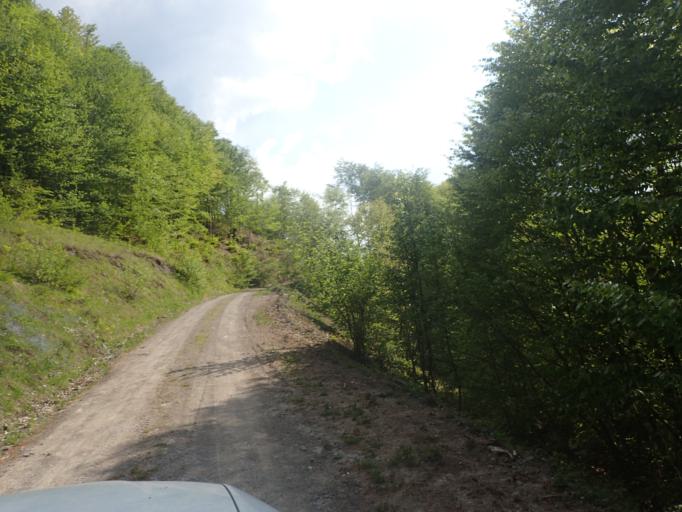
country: TR
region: Ordu
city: Akkus
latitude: 40.8347
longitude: 36.9749
